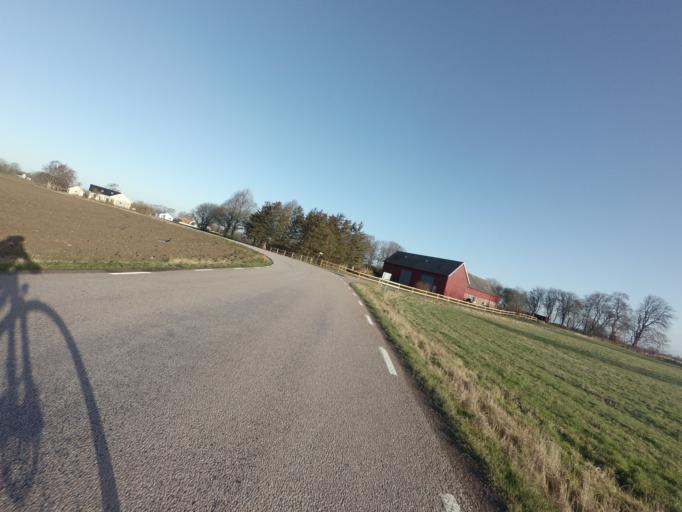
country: SE
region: Skane
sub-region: Helsingborg
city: Odakra
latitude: 56.1132
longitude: 12.6827
